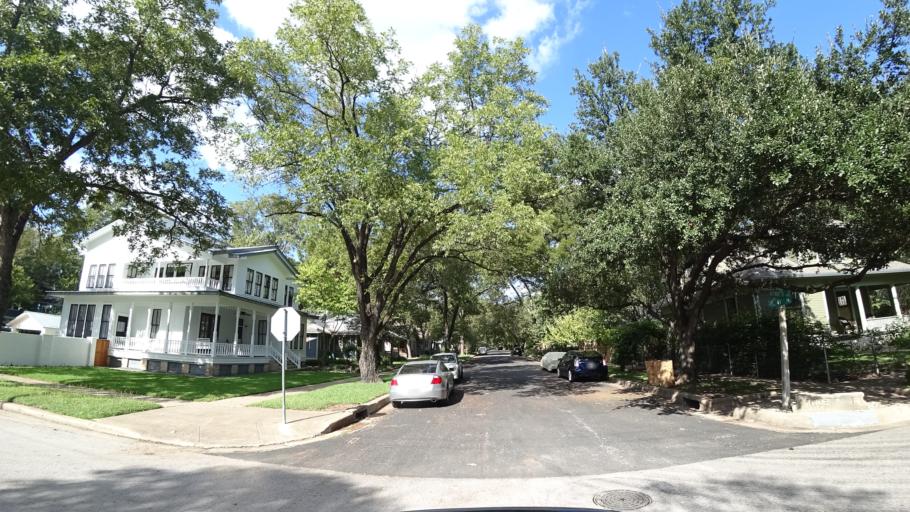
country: US
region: Texas
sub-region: Travis County
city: Austin
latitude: 30.3046
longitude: -97.7322
